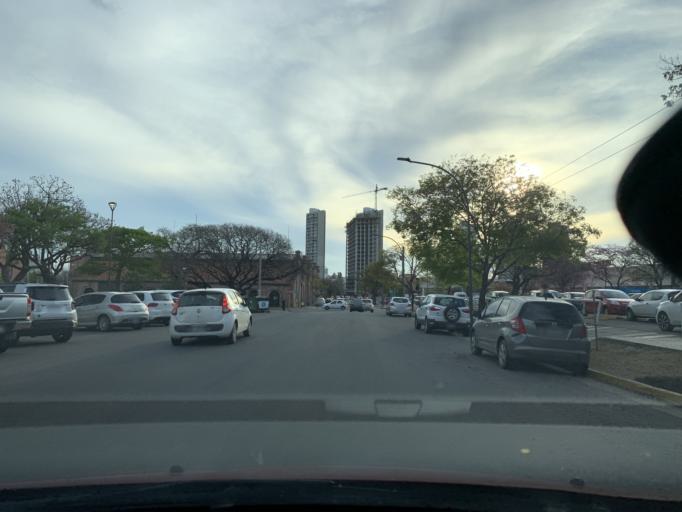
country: AR
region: Cordoba
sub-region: Departamento de Capital
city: Cordoba
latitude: -31.4086
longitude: -64.1684
